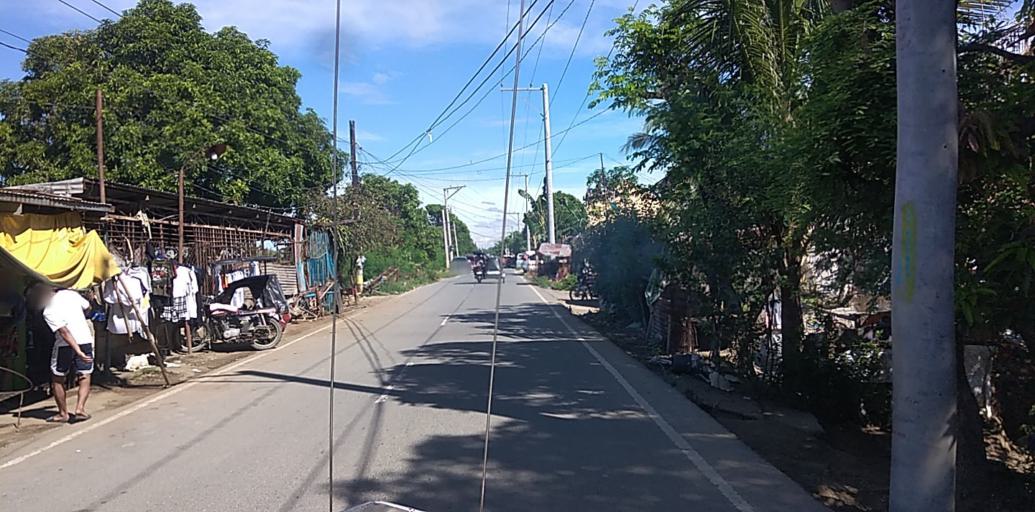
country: PH
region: Central Luzon
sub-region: Province of Pampanga
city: Candaba
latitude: 15.0913
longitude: 120.8117
